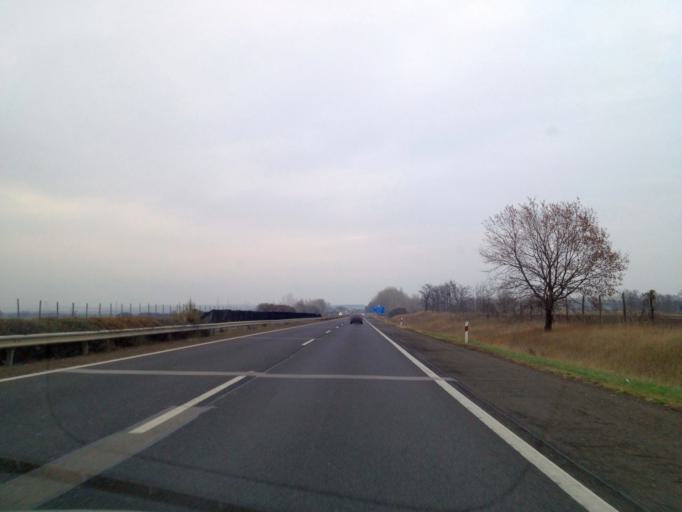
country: HU
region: Heves
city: Hatvan
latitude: 47.6784
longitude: 19.6522
